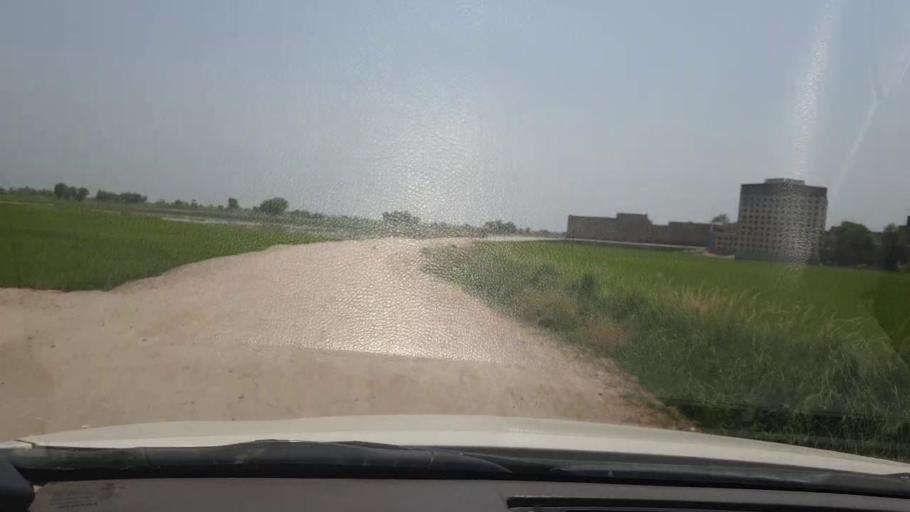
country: PK
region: Sindh
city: Garhi Yasin
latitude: 27.9268
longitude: 68.5496
